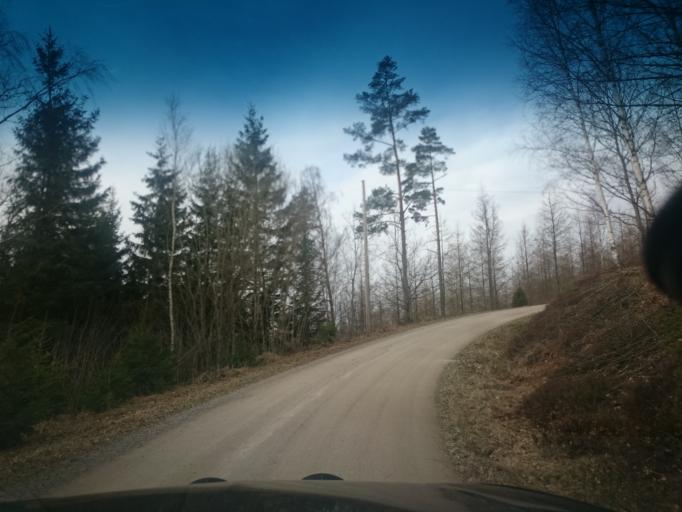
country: SE
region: Joenkoeping
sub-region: Vetlanda Kommun
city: Vetlanda
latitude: 57.3290
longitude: 15.1573
